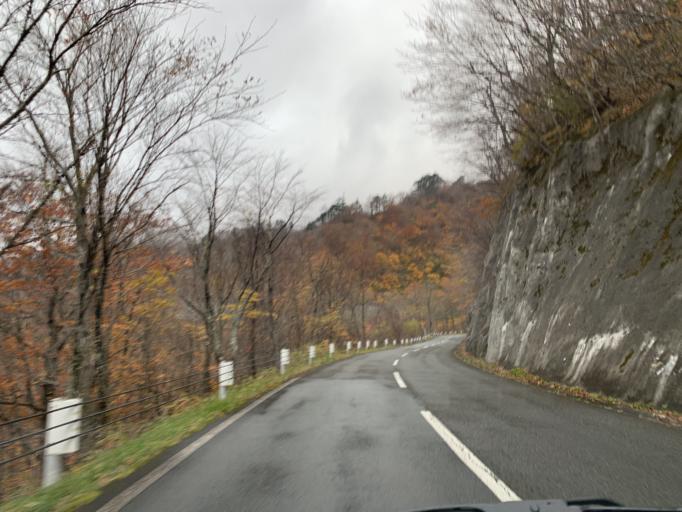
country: JP
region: Iwate
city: Mizusawa
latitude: 39.1237
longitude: 140.8285
